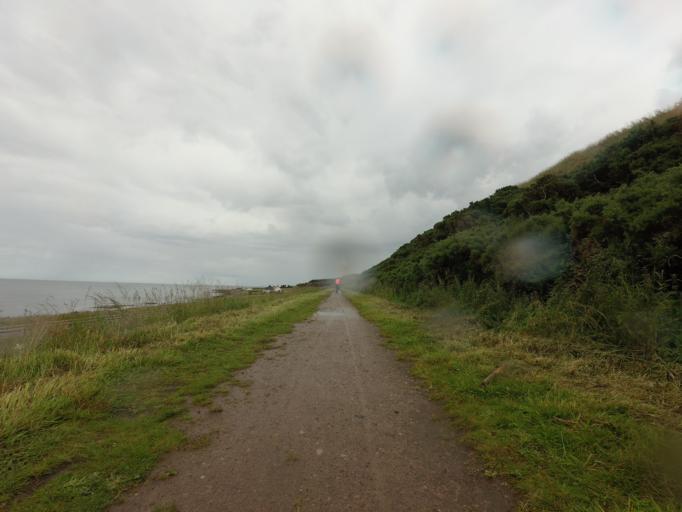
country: GB
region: Scotland
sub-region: Moray
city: Buckie
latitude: 57.6673
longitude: -3.0009
